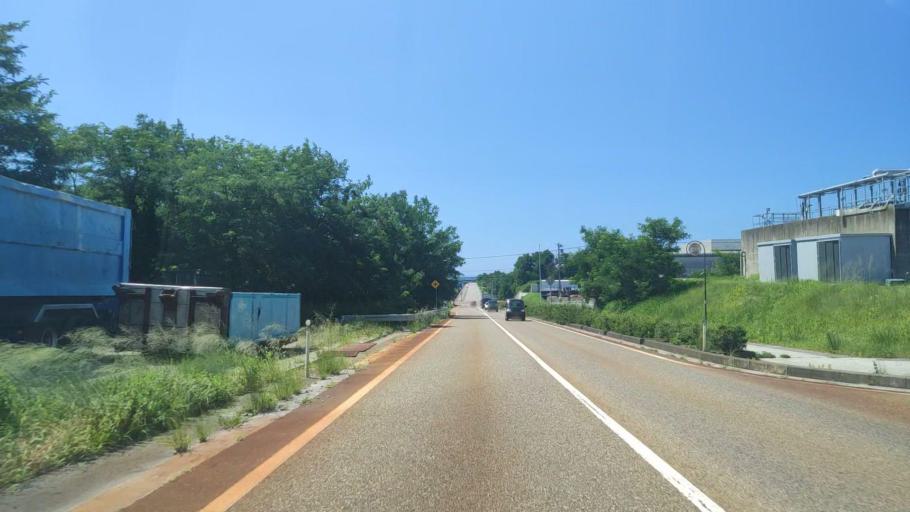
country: JP
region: Ishikawa
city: Kanazawa-shi
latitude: 36.6257
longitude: 136.6138
